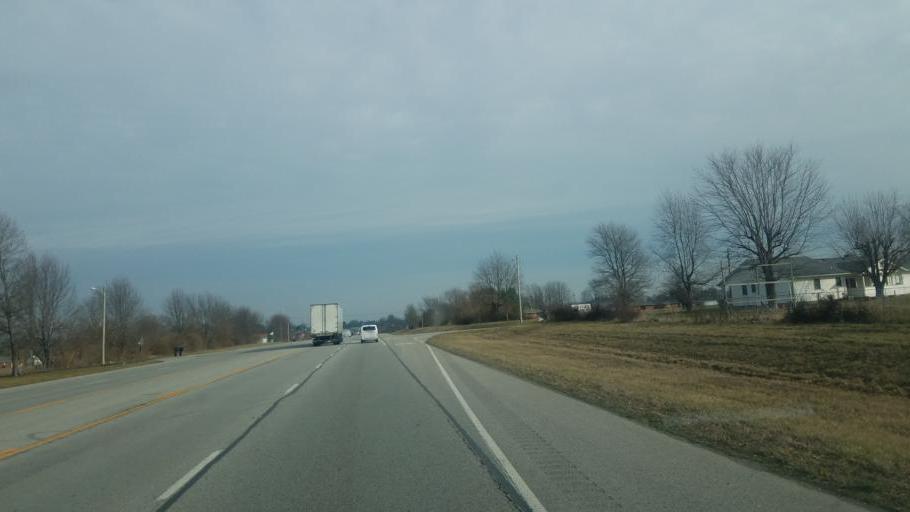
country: US
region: Kentucky
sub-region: Boyle County
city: Junction City
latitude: 37.5869
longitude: -84.7833
